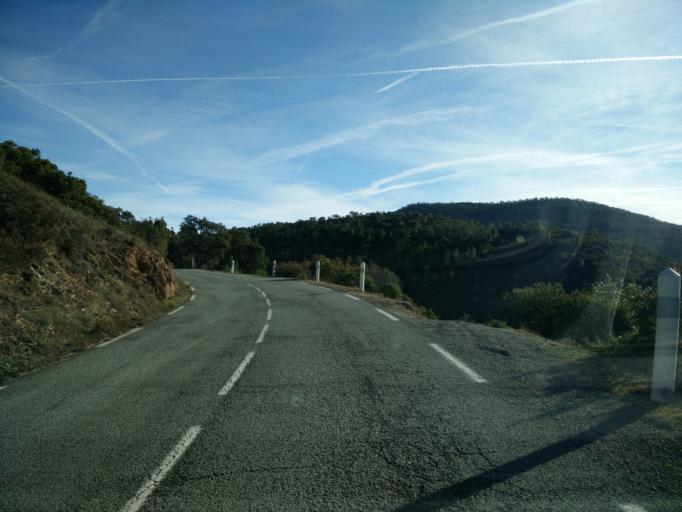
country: FR
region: Provence-Alpes-Cote d'Azur
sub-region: Departement du Var
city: Saint-Raphael
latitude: 43.5008
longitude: 6.7824
